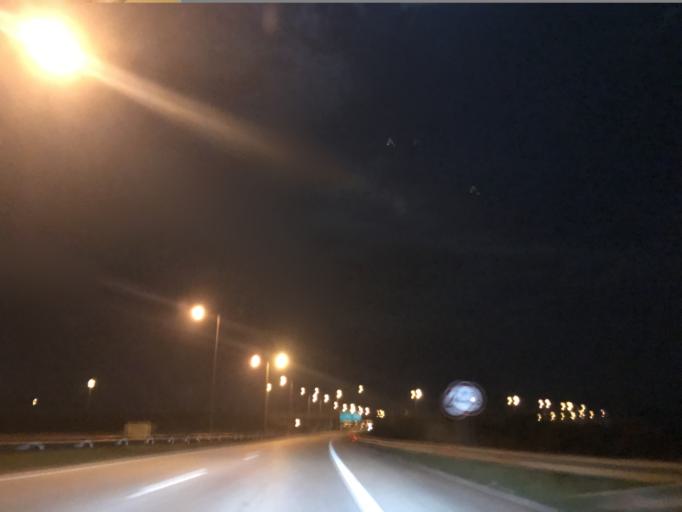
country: TR
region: Hatay
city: Mahmutlar
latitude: 36.9646
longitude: 36.1092
